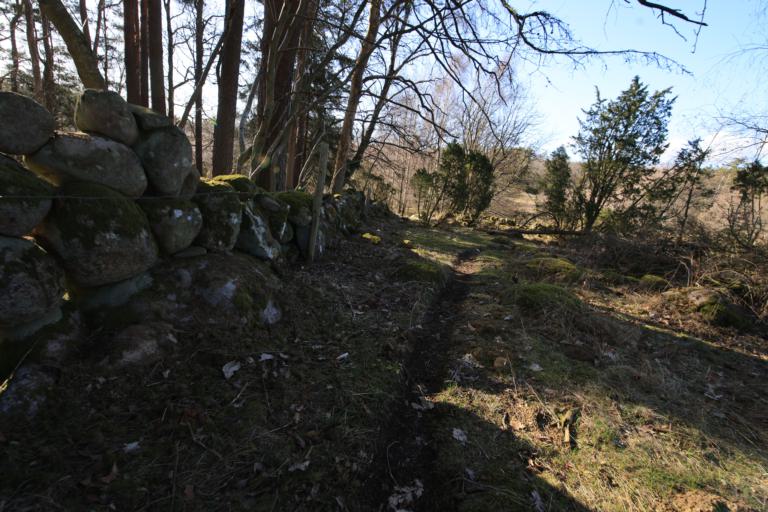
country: SE
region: Halland
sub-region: Varbergs Kommun
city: Varberg
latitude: 57.1674
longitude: 12.2651
